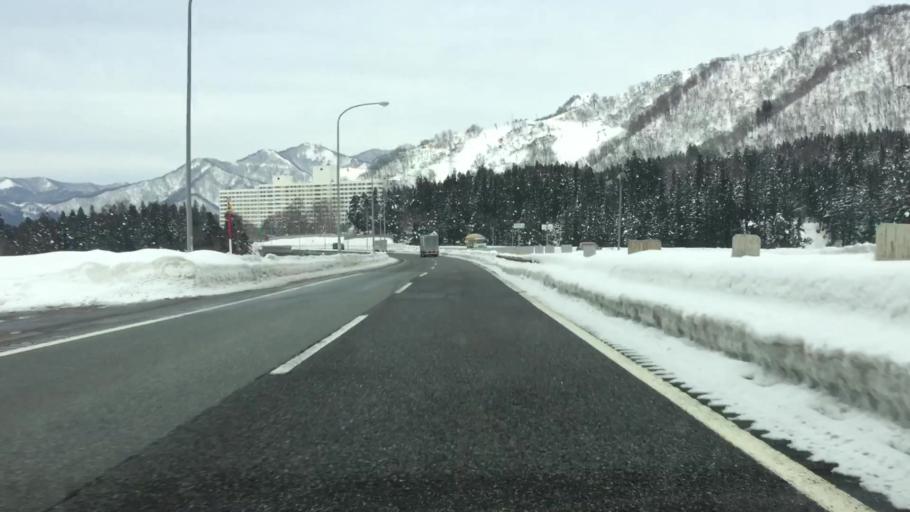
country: JP
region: Niigata
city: Shiozawa
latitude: 36.8991
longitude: 138.8464
